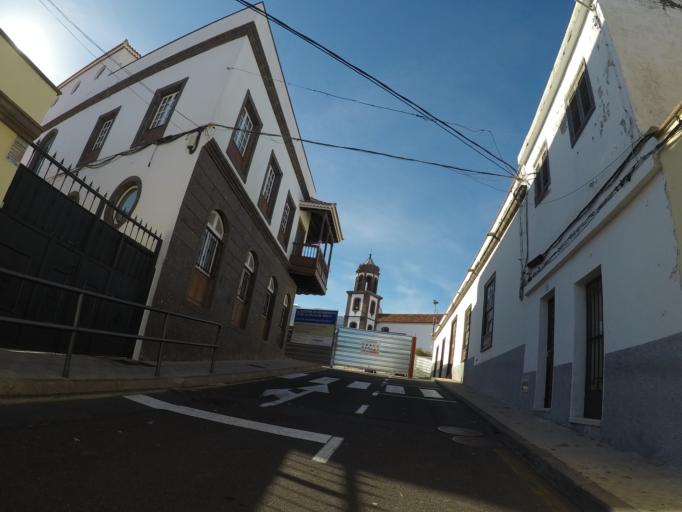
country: ES
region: Canary Islands
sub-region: Provincia de Santa Cruz de Tenerife
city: Lomo de Arico
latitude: 28.1658
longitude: -16.5007
